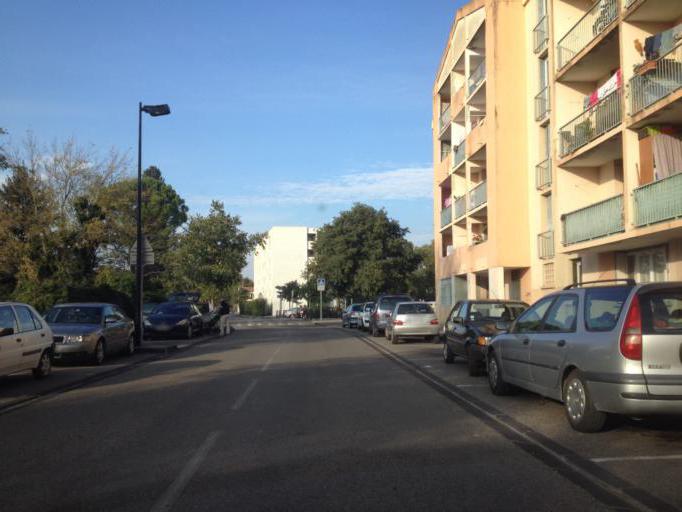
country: FR
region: Provence-Alpes-Cote d'Azur
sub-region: Departement du Vaucluse
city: Orange
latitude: 44.1306
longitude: 4.8001
